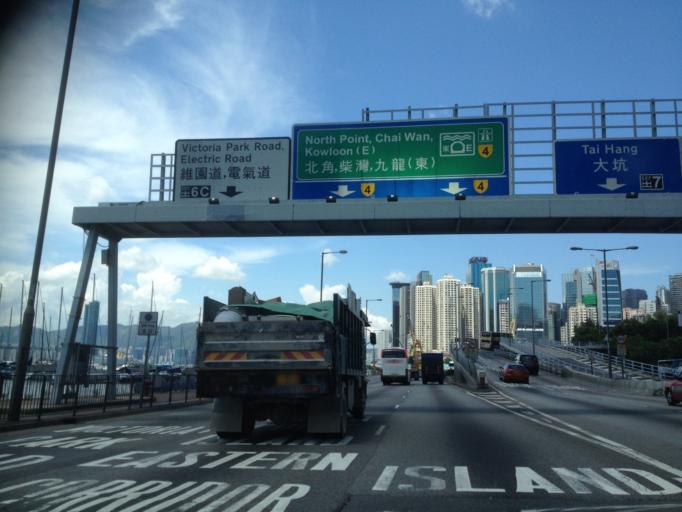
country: HK
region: Wanchai
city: Wan Chai
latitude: 22.2828
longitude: 114.1844
